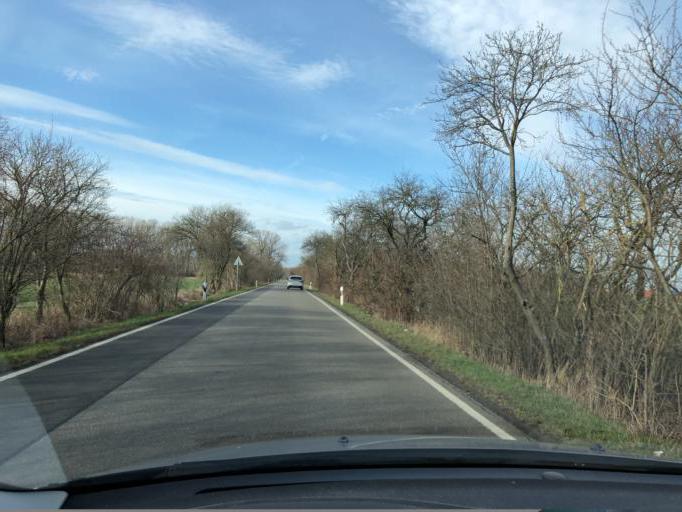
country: DE
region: Thuringia
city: Niederzimmern
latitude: 51.0011
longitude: 11.1669
